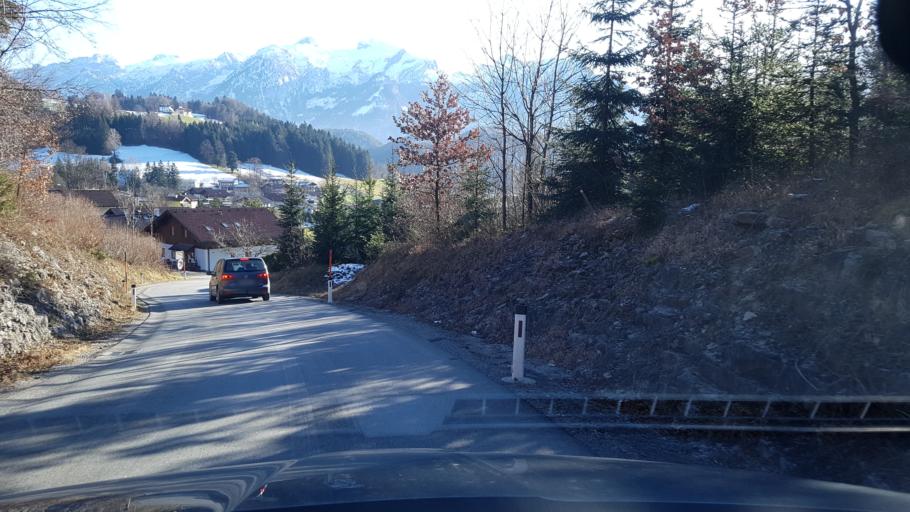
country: AT
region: Salzburg
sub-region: Politischer Bezirk Hallein
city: Golling an der Salzach
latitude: 47.6193
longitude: 13.1730
